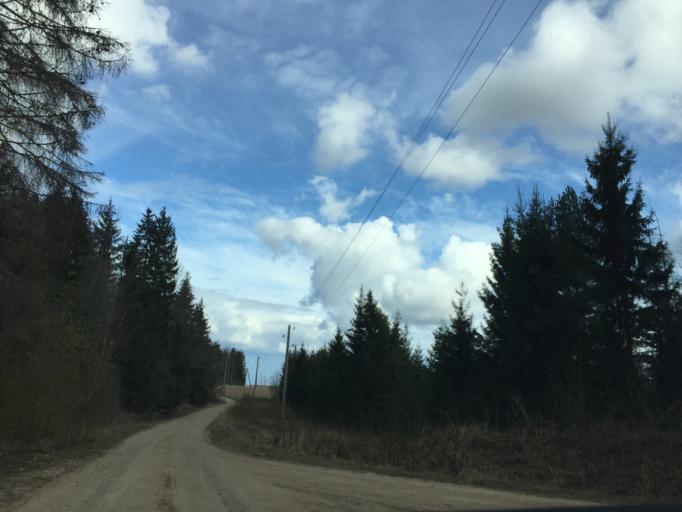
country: LV
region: Burtnieki
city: Matisi
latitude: 57.6145
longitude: 25.0055
